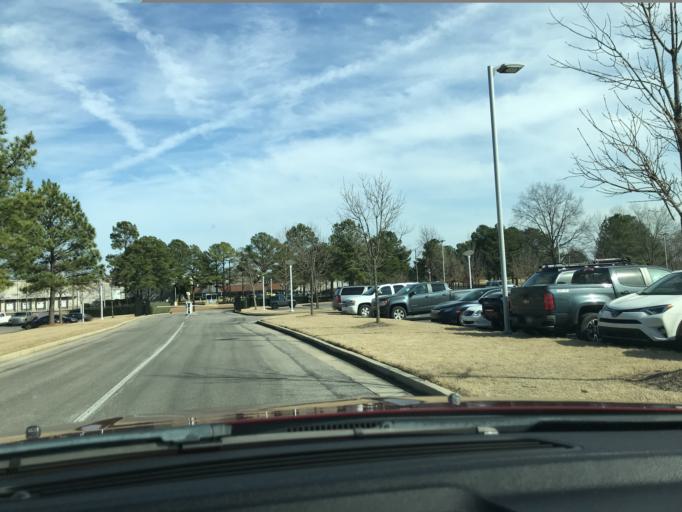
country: US
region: Tennessee
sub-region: Shelby County
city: Germantown
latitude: 35.0496
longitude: -89.7852
